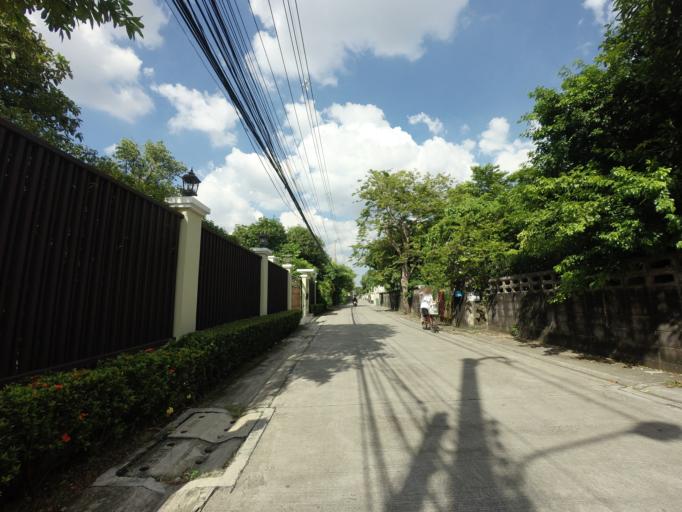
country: TH
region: Bangkok
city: Wang Thonglang
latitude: 13.7874
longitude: 100.5954
